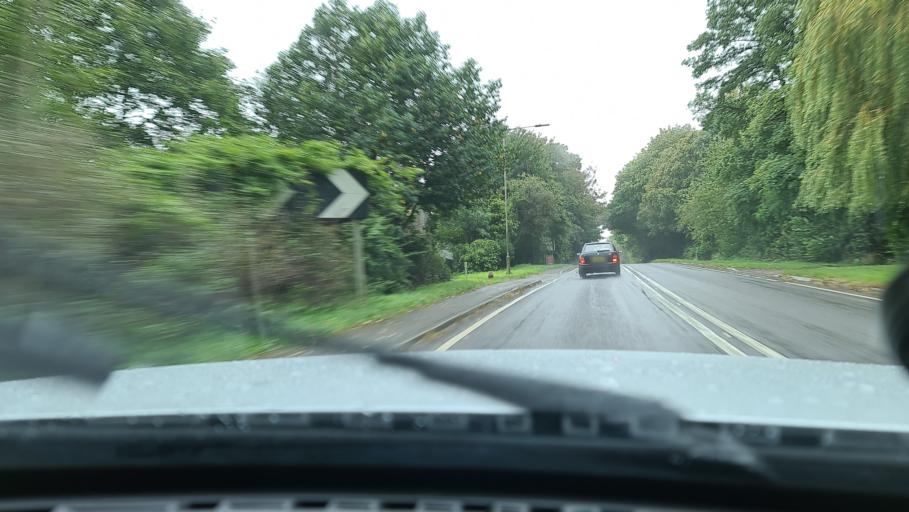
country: GB
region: England
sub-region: Oxfordshire
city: Adderbury
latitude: 52.0130
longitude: -1.3093
